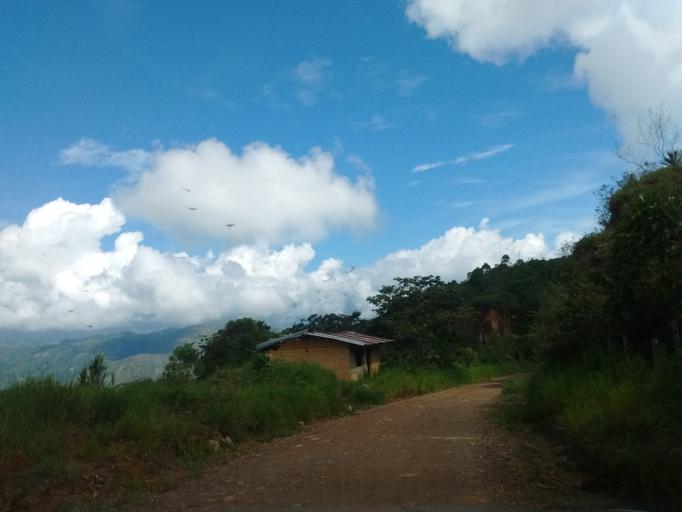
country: CO
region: Cauca
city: Morales
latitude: 2.6862
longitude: -76.7321
